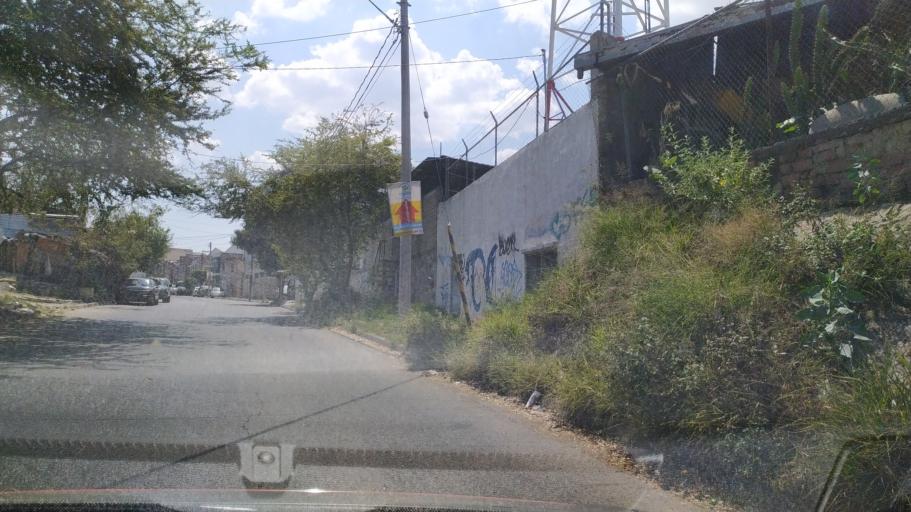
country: MX
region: Jalisco
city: Guadalajara
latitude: 20.6185
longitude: -103.3906
